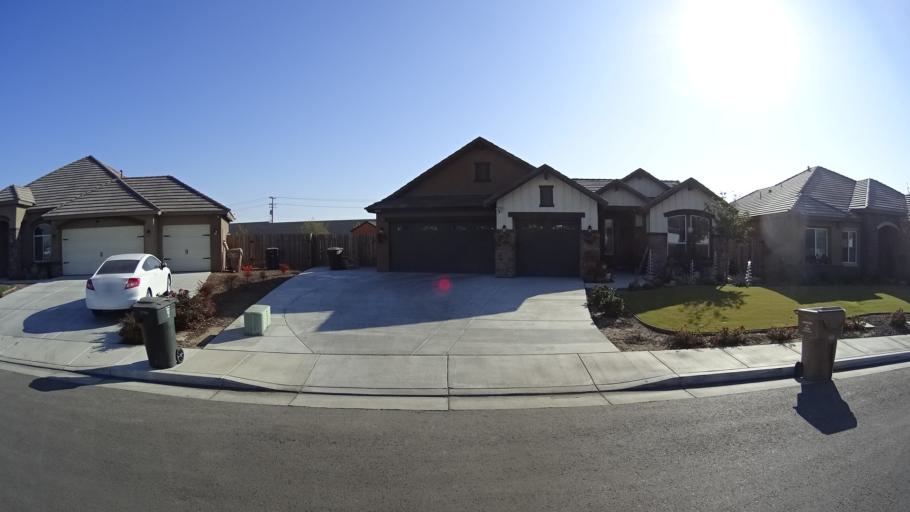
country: US
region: California
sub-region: Kern County
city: Greenacres
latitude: 35.3769
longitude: -119.1020
